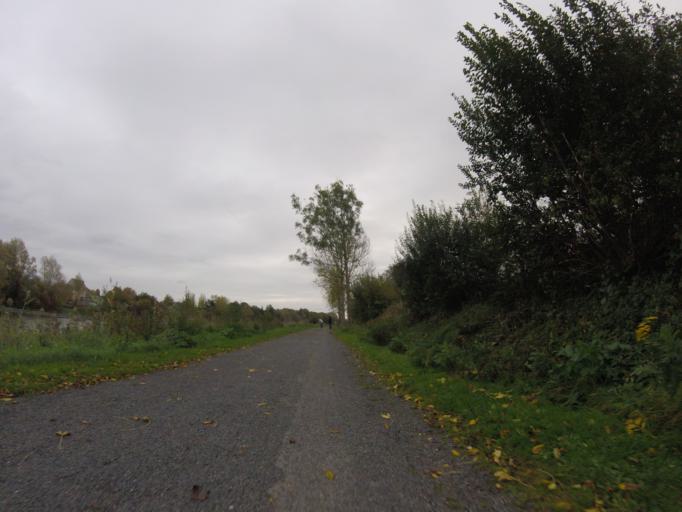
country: FR
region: Nord-Pas-de-Calais
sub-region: Departement du Nord
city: Quesnoy-sur-Deule
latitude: 50.7079
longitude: 3.0082
